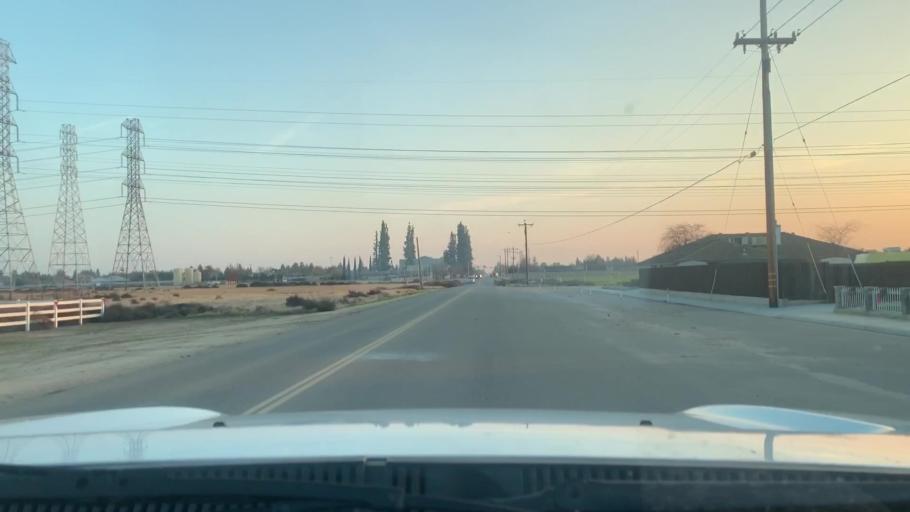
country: US
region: California
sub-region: Kern County
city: Rosedale
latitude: 35.3880
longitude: -119.1811
